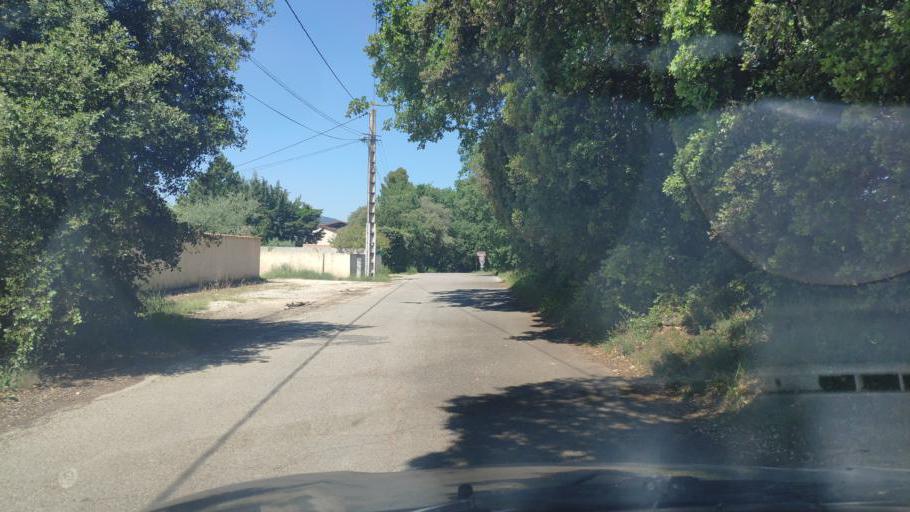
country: FR
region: Provence-Alpes-Cote d'Azur
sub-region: Departement du Vaucluse
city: Carpentras
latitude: 44.0848
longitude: 5.0568
